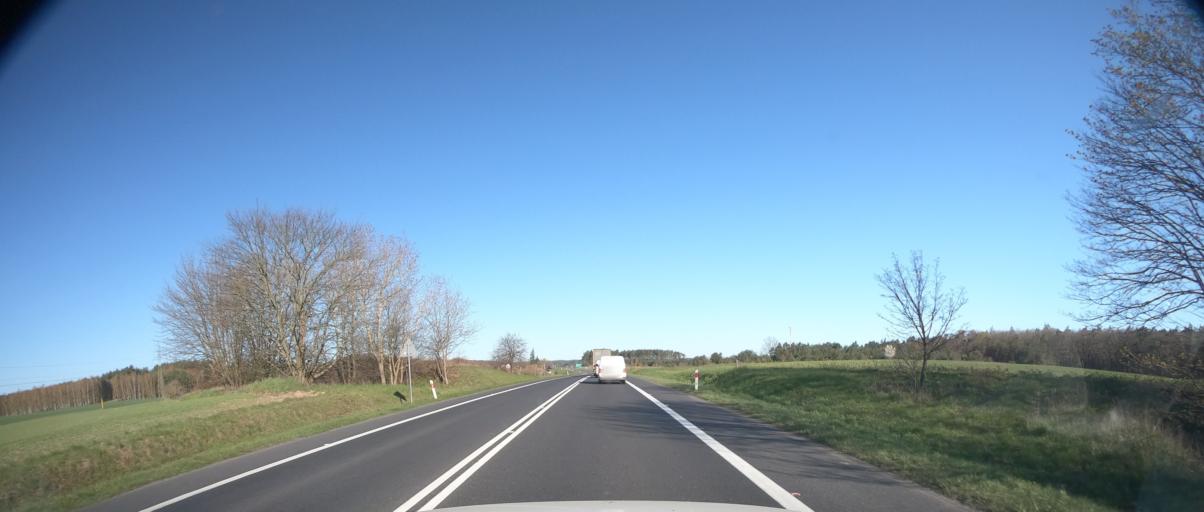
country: PL
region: West Pomeranian Voivodeship
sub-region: Powiat kamienski
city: Wolin
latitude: 53.8650
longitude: 14.5513
